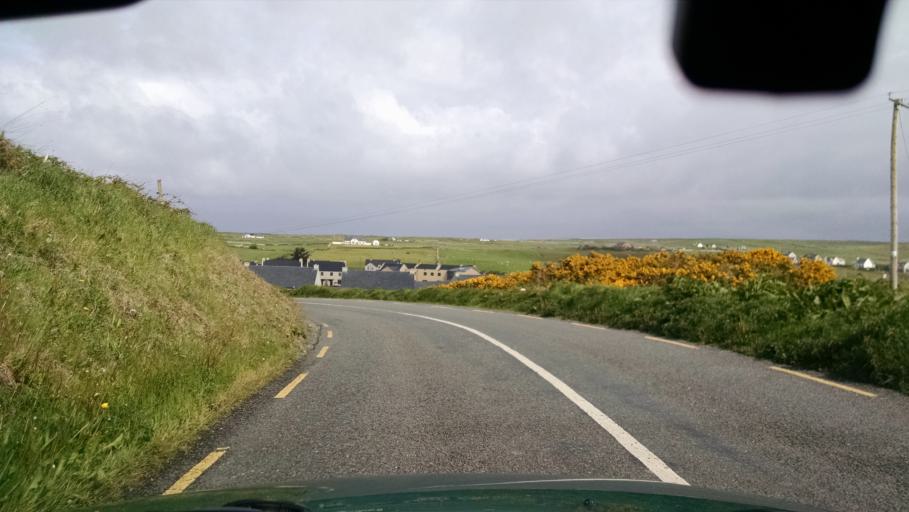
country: IE
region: Connaught
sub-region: County Galway
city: Bearna
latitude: 53.0147
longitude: -9.3730
